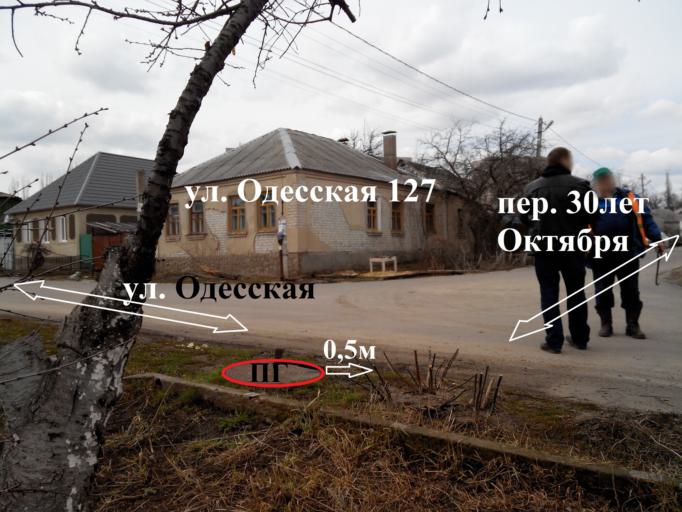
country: RU
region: Voronezj
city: Voronezh
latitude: 51.6367
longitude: 39.1586
